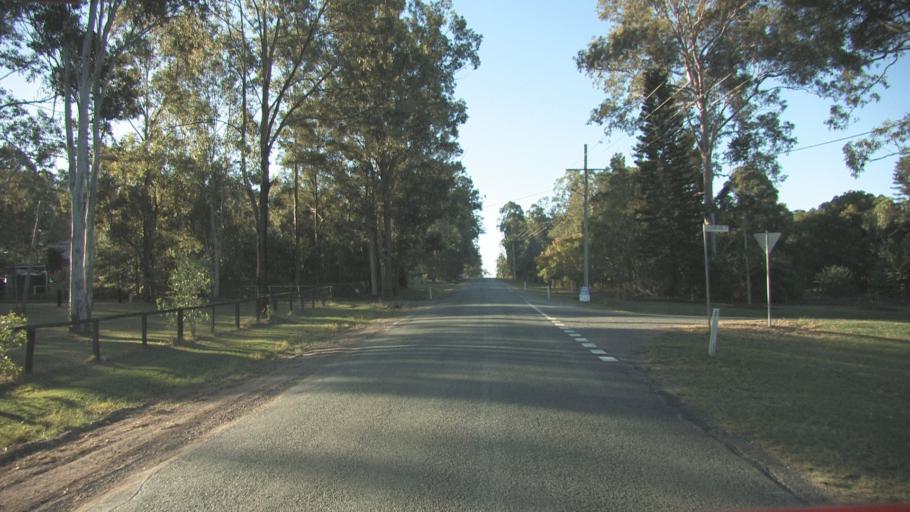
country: AU
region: Queensland
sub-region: Logan
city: Chambers Flat
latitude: -27.7803
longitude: 153.1356
